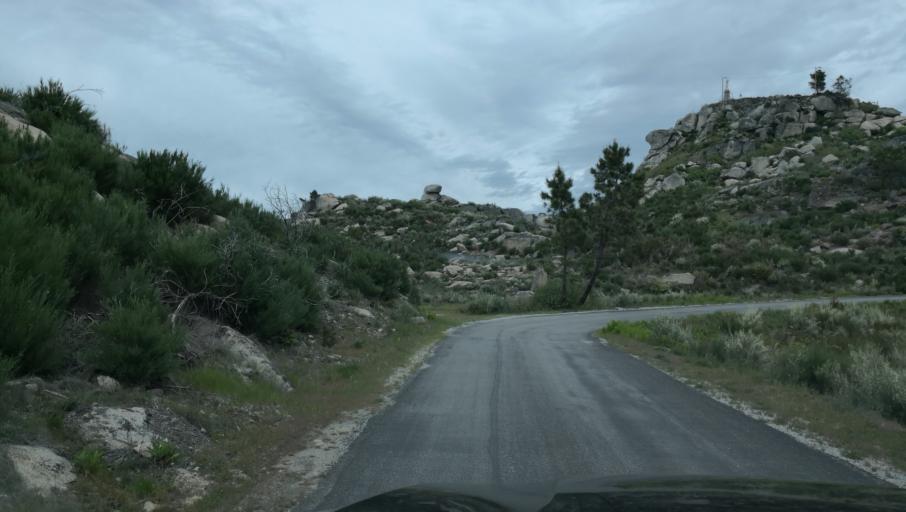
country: PT
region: Vila Real
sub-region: Vila Real
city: Vila Real
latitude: 41.3746
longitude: -7.6865
